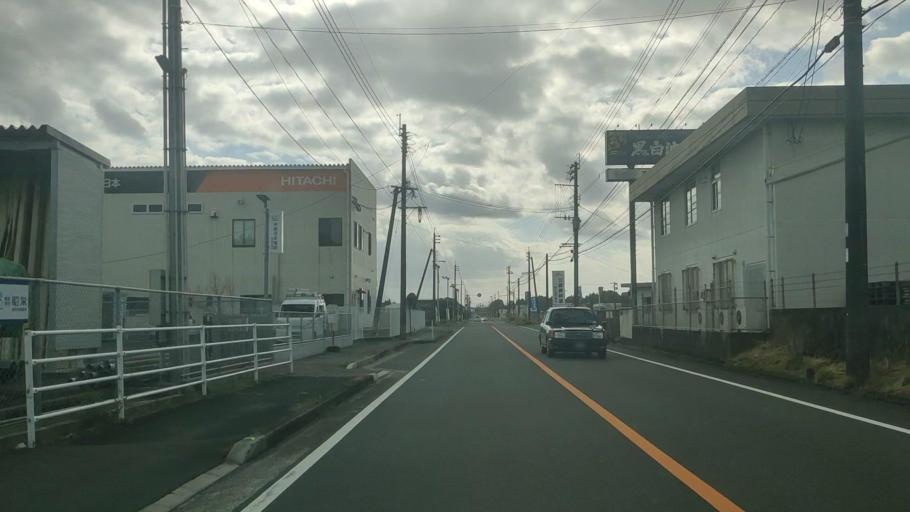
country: JP
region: Kagoshima
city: Kajiki
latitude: 31.7828
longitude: 130.7049
